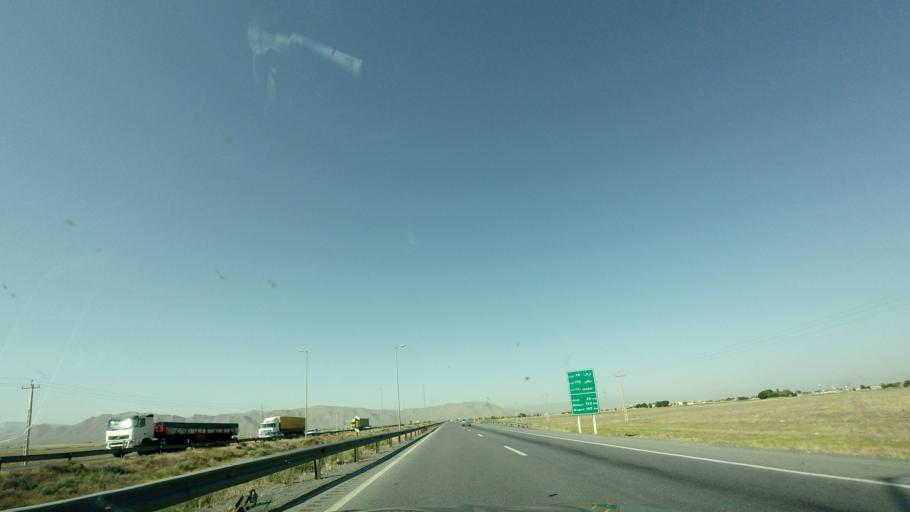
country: IR
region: Markazi
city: Ashtian
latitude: 34.1742
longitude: 50.0384
